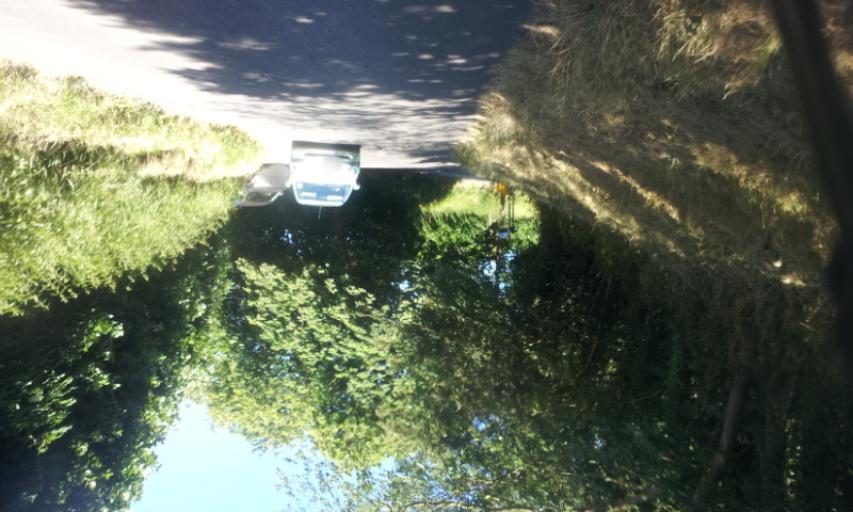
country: GB
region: England
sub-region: Kent
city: Teynham
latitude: 51.3474
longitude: 0.7799
